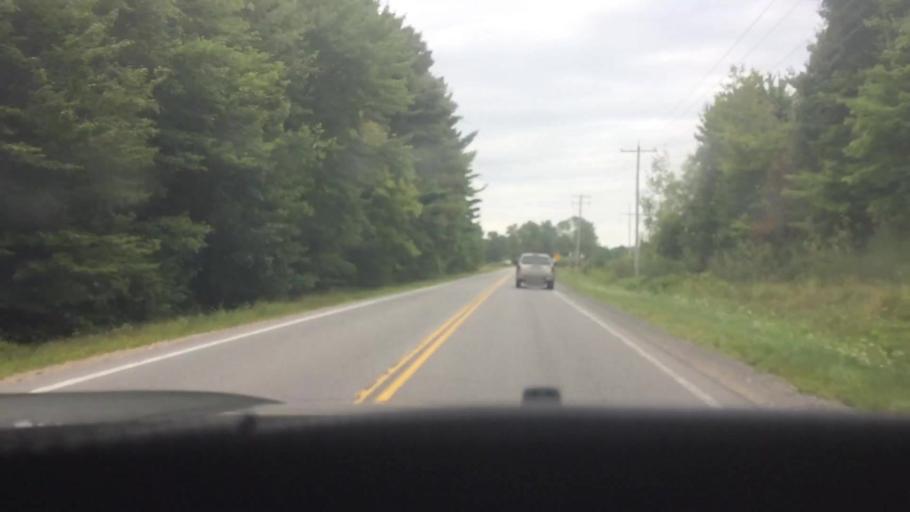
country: US
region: New York
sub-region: St. Lawrence County
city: Canton
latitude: 44.5090
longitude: -75.2100
